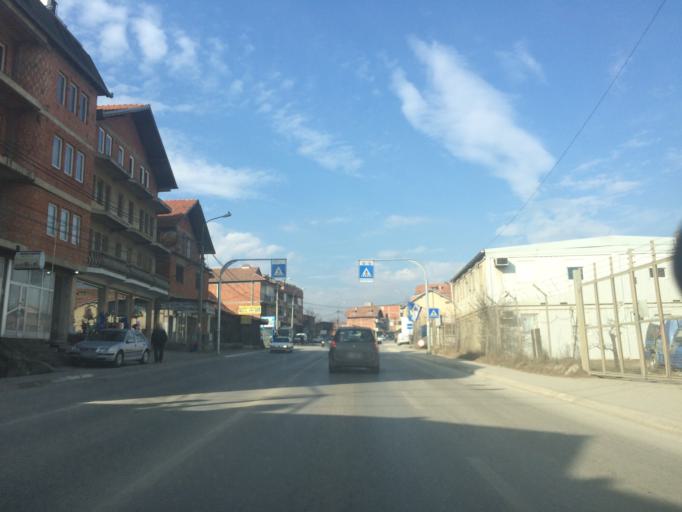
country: XK
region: Pristina
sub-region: Komuna e Prishtines
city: Pristina
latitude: 42.6812
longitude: 21.1597
